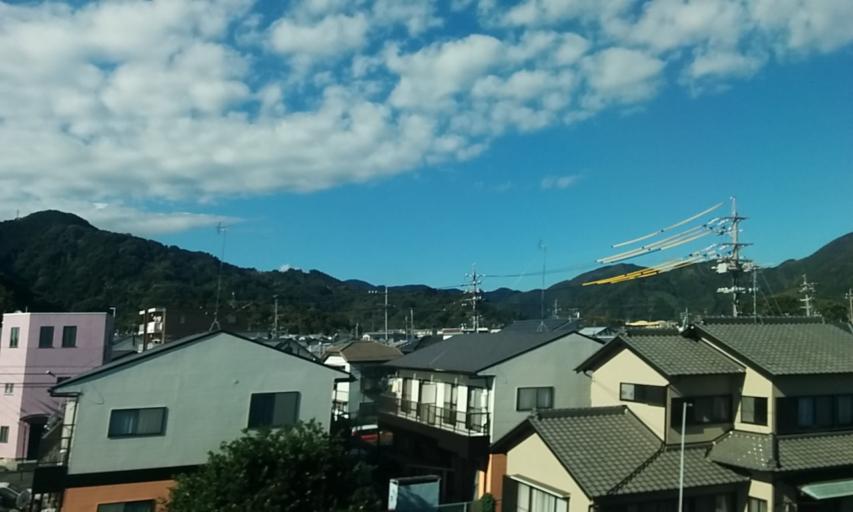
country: JP
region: Shizuoka
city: Shizuoka-shi
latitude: 34.9398
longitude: 138.3630
